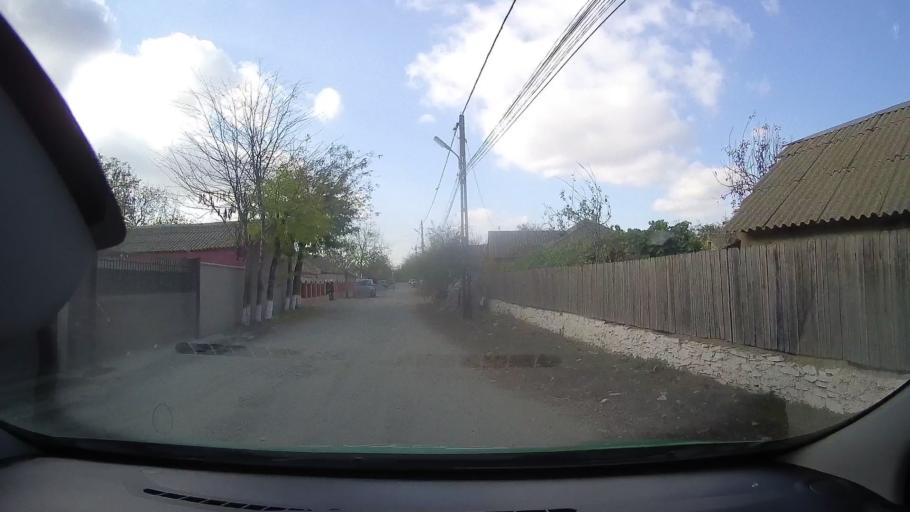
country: RO
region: Constanta
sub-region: Comuna Sacele
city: Sacele
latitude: 44.4896
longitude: 28.6359
